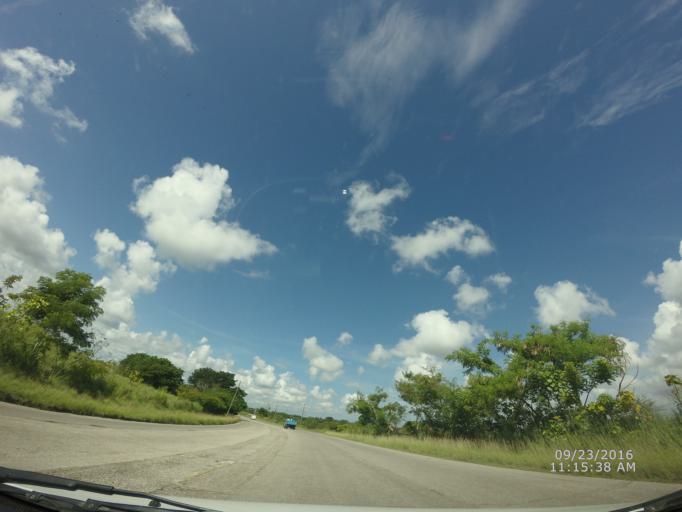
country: CU
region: La Habana
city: Arroyo Naranjo
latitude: 23.0401
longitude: -82.3124
